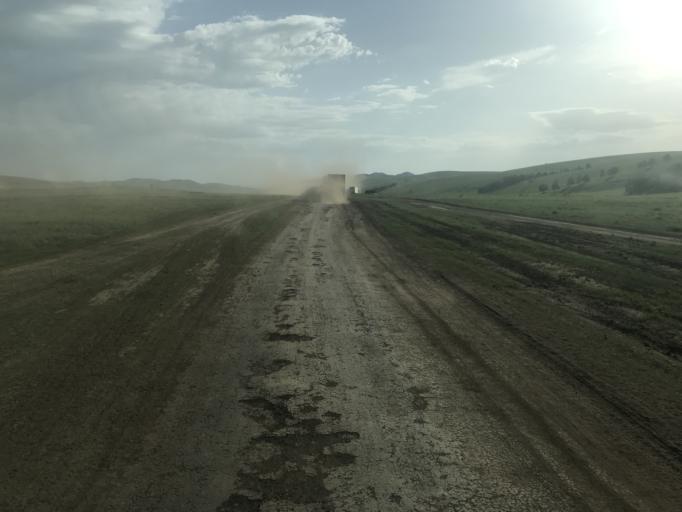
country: MN
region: Central Aimak
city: Javhlant
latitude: 48.6552
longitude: 106.1152
